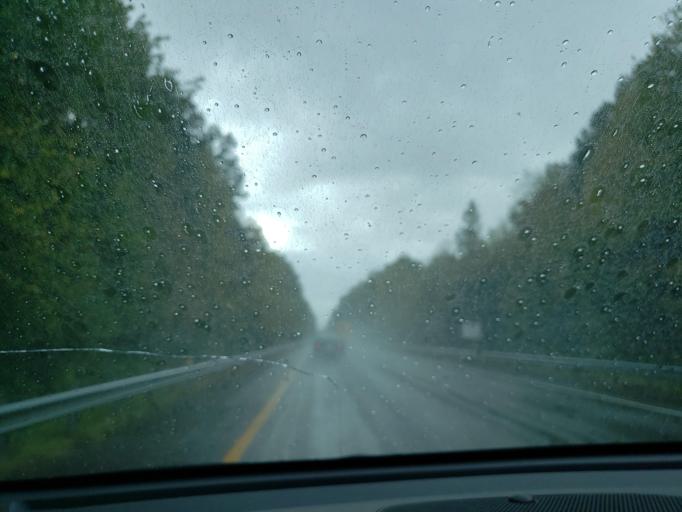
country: US
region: Virginia
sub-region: Mecklenburg County
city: South Hill
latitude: 36.7028
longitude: -78.1183
